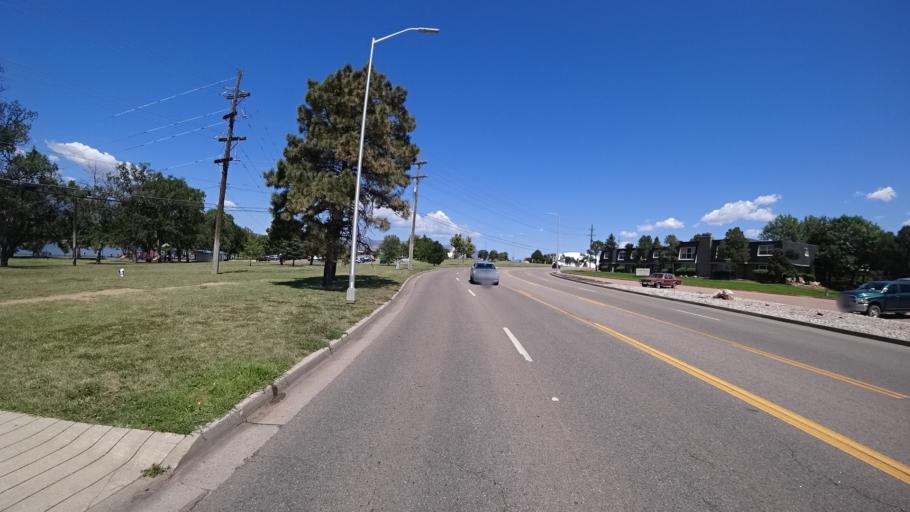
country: US
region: Colorado
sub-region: El Paso County
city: Colorado Springs
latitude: 38.8254
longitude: -104.7946
